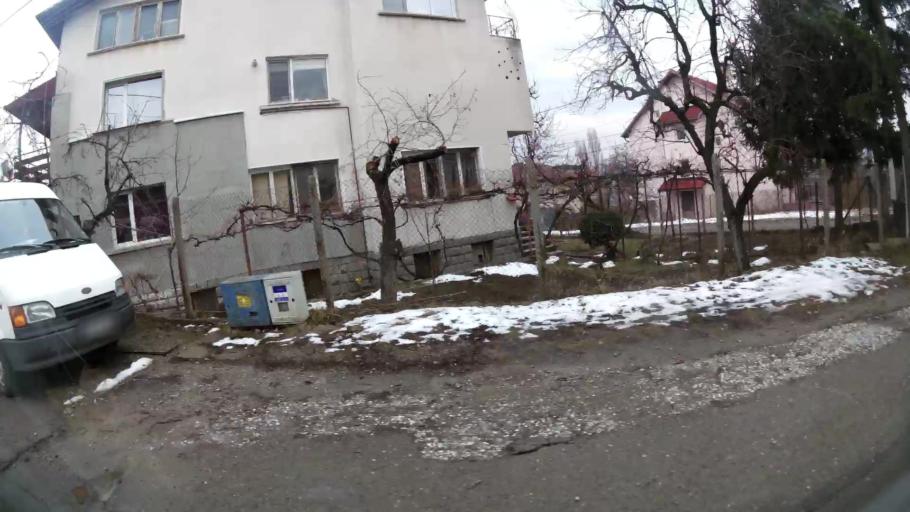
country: BG
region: Sofia-Capital
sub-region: Stolichna Obshtina
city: Sofia
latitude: 42.6670
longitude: 23.2463
